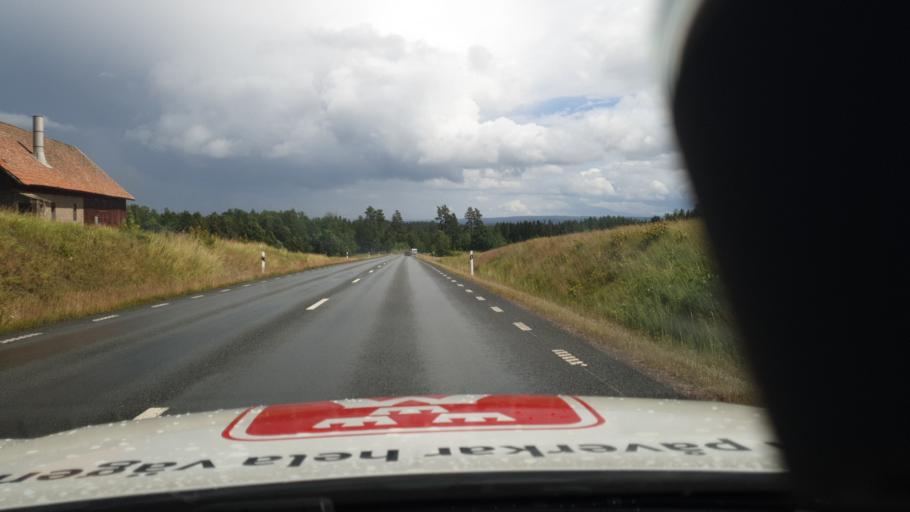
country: SE
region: Vaestra Goetaland
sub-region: Tidaholms Kommun
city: Tidaholm
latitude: 58.1286
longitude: 13.8180
